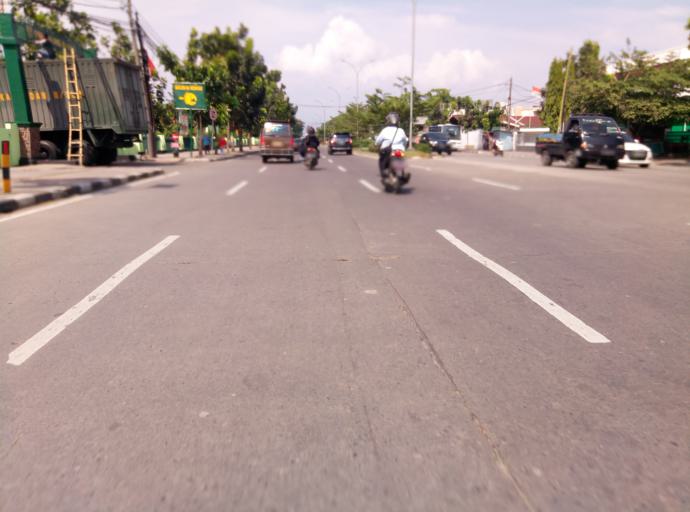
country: ID
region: West Java
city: Bandung
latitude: -6.9383
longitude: 107.6425
